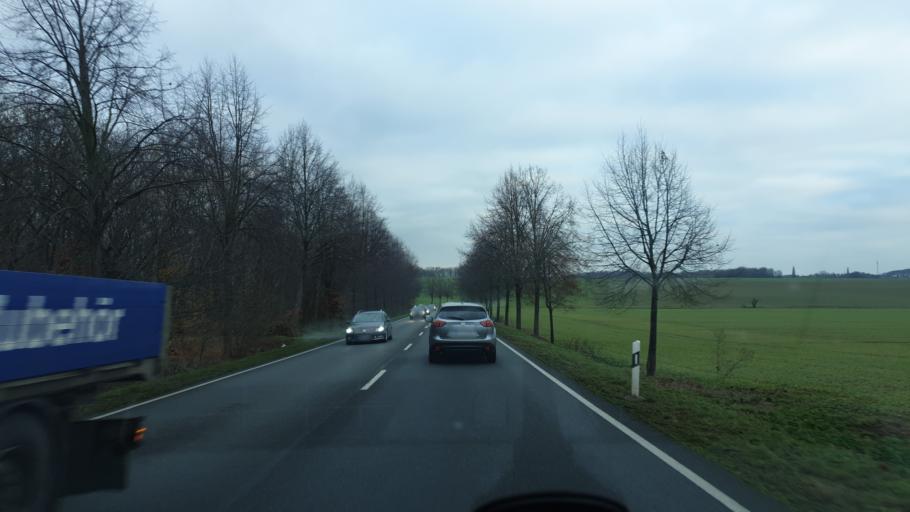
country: DE
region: Saxony-Anhalt
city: Stossen
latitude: 51.1208
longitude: 11.9094
